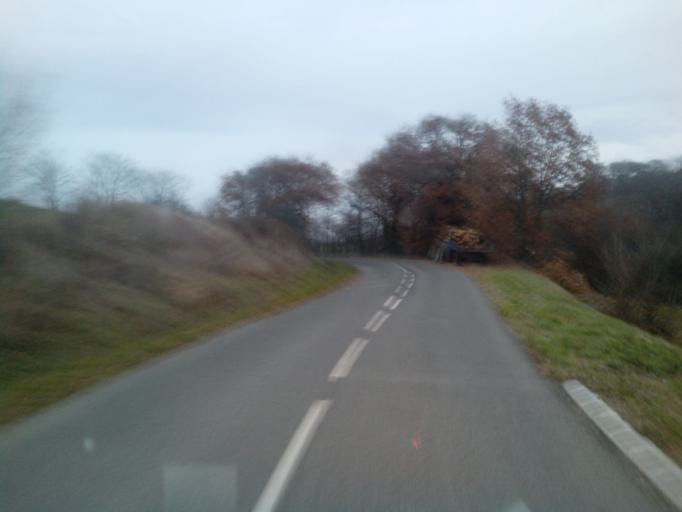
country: FR
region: Languedoc-Roussillon
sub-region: Departement de l'Aude
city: Belpech
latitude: 43.2612
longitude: 1.7440
